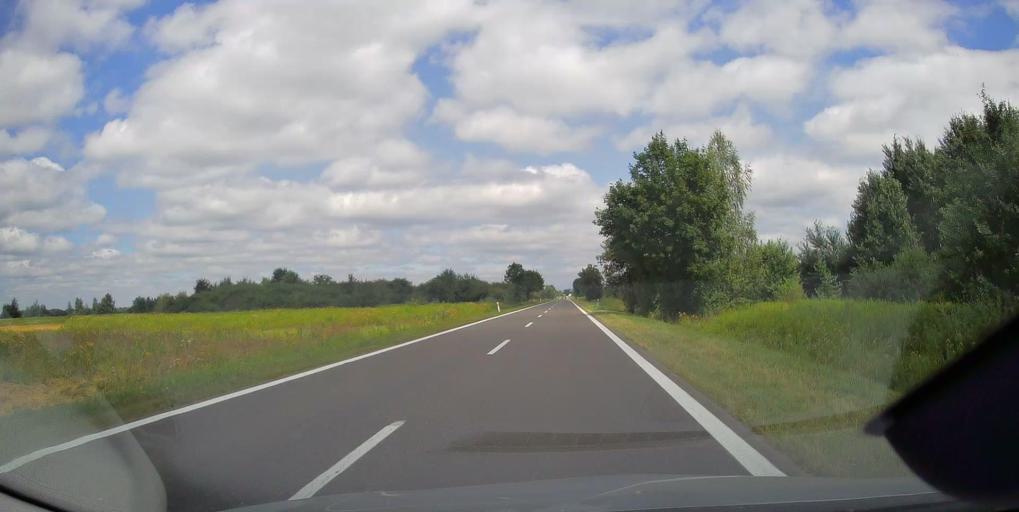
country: PL
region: Subcarpathian Voivodeship
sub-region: Powiat tarnobrzeski
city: Baranow Sandomierski
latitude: 50.4930
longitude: 21.5699
